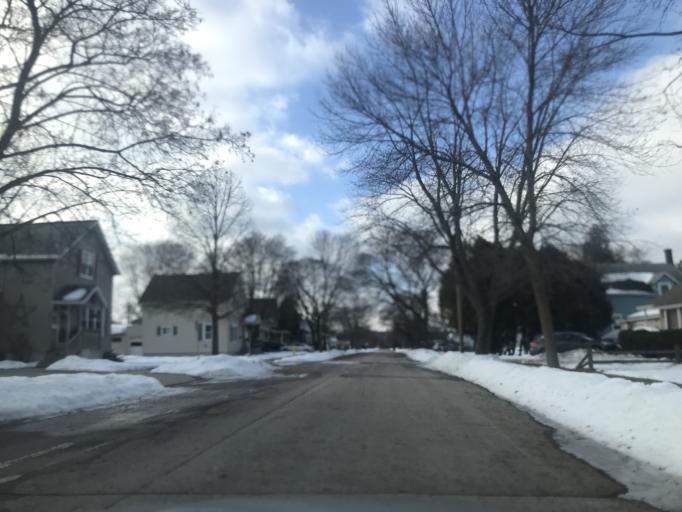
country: US
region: Wisconsin
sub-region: Marinette County
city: Marinette
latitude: 45.1012
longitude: -87.6423
